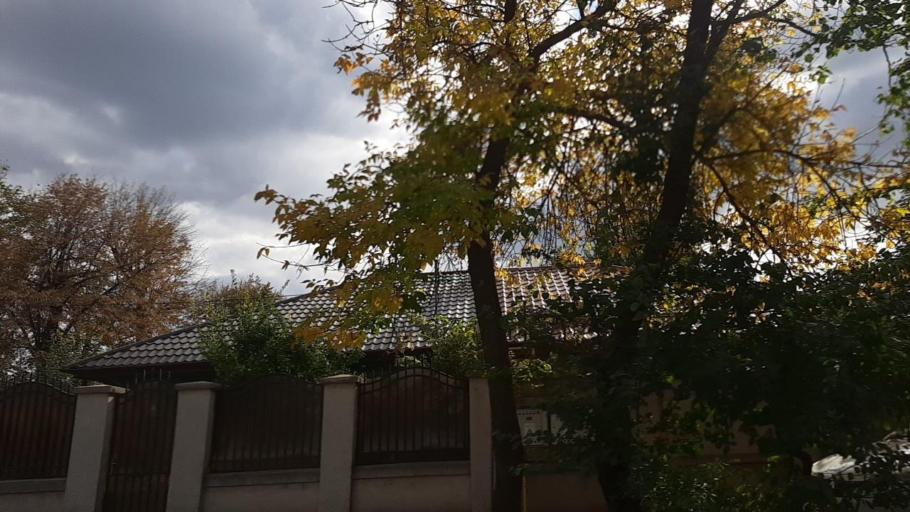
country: RO
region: Galati
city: Galati
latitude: 45.4482
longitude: 28.0302
